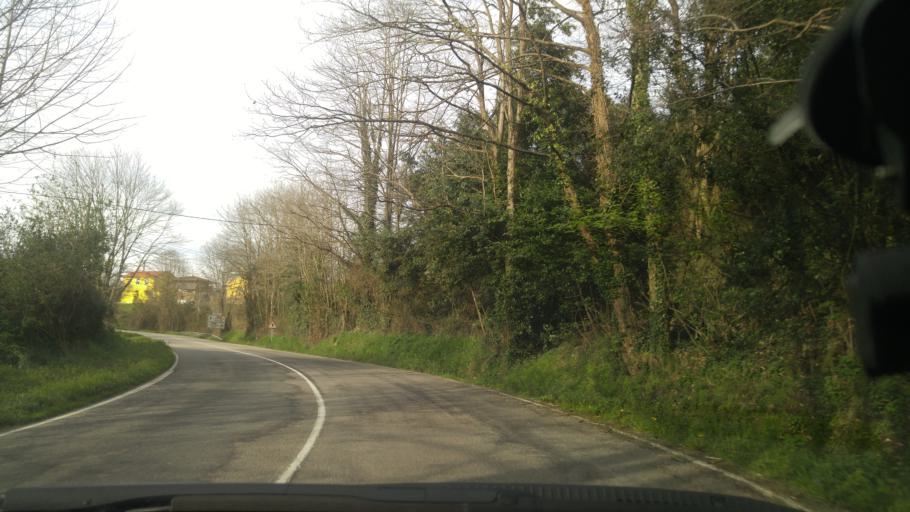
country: ES
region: Asturias
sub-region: Province of Asturias
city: Llanera
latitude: 43.4611
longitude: -5.8504
